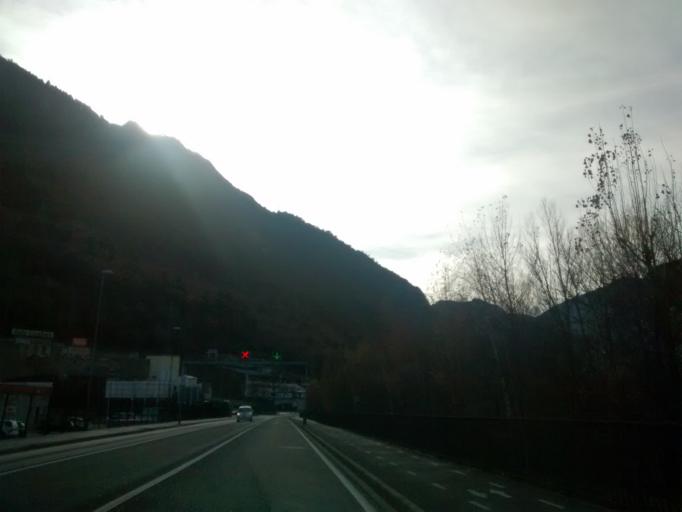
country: AD
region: Andorra la Vella
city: Andorra la Vella
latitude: 42.4997
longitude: 1.5119
